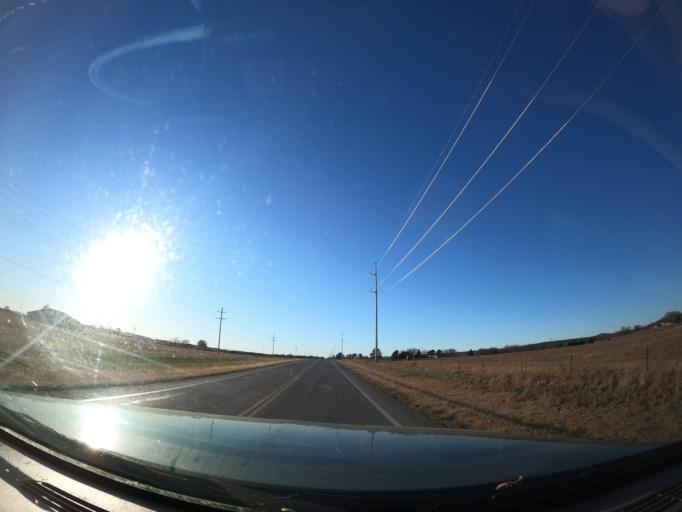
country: US
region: Oklahoma
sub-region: Latimer County
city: Wilburton
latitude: 34.9129
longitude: -95.4124
